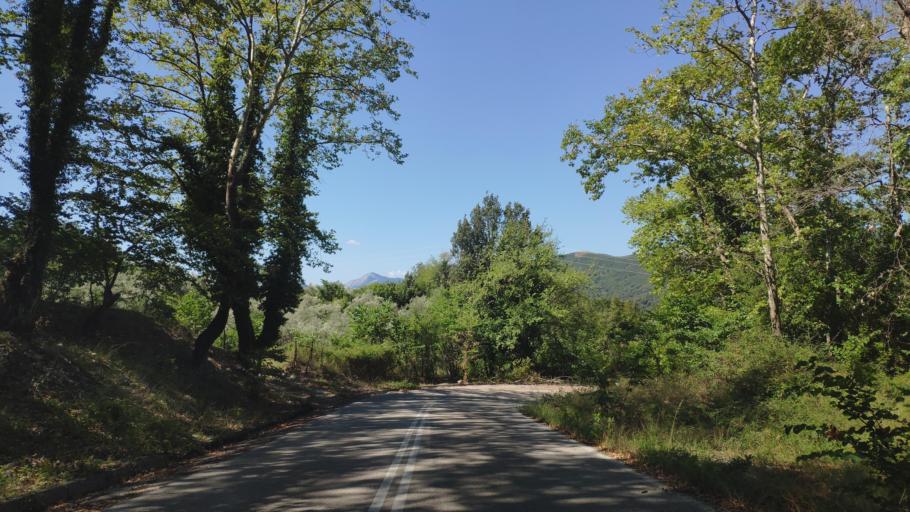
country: GR
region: Central Greece
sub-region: Nomos Evrytanias
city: Kerasochori
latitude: 39.0219
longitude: 21.6006
